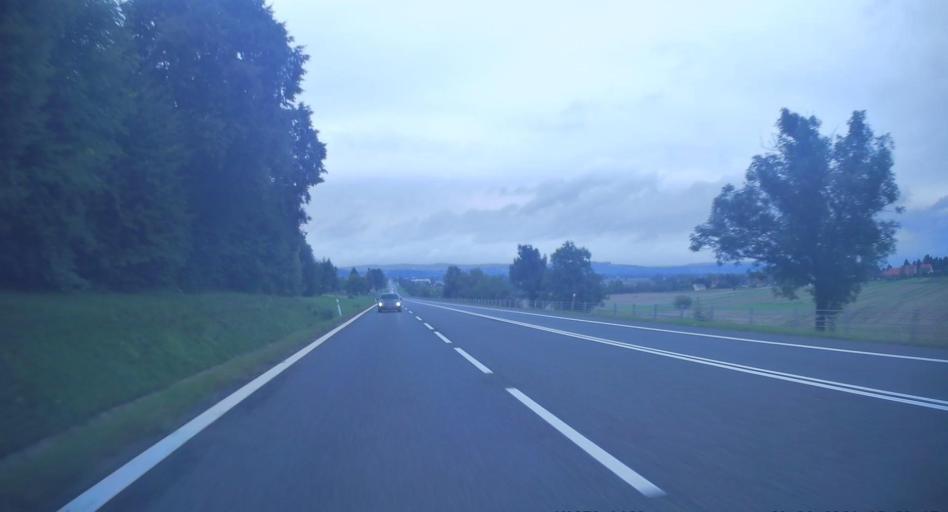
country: PL
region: Lesser Poland Voivodeship
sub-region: Powiat wielicki
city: Szarow
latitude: 49.9798
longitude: 20.2622
